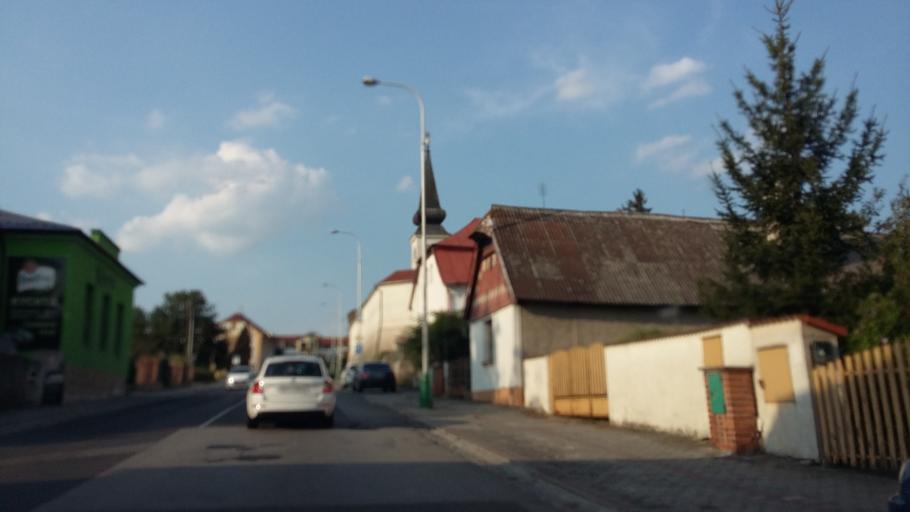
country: CZ
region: Central Bohemia
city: Kosmonosy
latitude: 50.4376
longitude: 14.9295
